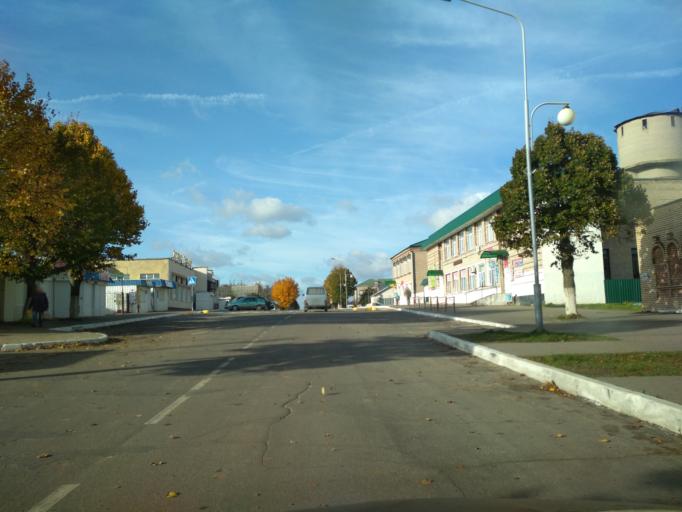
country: BY
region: Minsk
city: Mar''ina Horka
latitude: 53.5075
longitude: 28.1494
